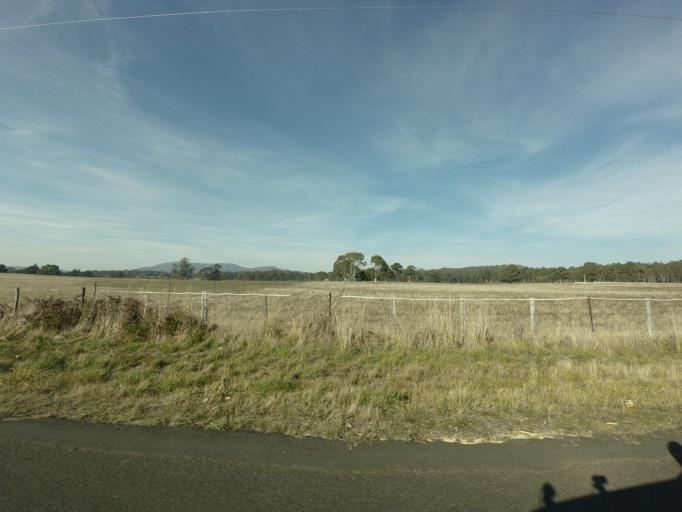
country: AU
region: Tasmania
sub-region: Sorell
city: Sorell
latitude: -42.4791
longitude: 147.4579
